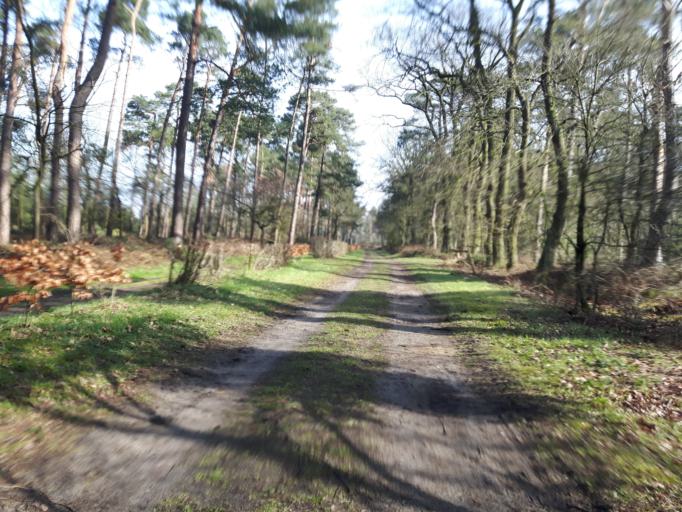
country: DE
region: North Rhine-Westphalia
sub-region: Regierungsbezirk Munster
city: Dulmen
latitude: 51.7915
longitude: 7.2391
